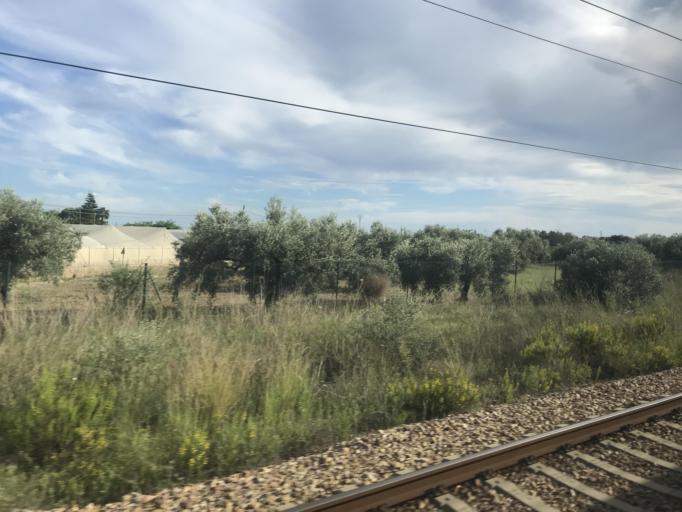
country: ES
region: Valencia
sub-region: Provincia de Castello
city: Benicarlo
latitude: 40.4371
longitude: 0.4236
